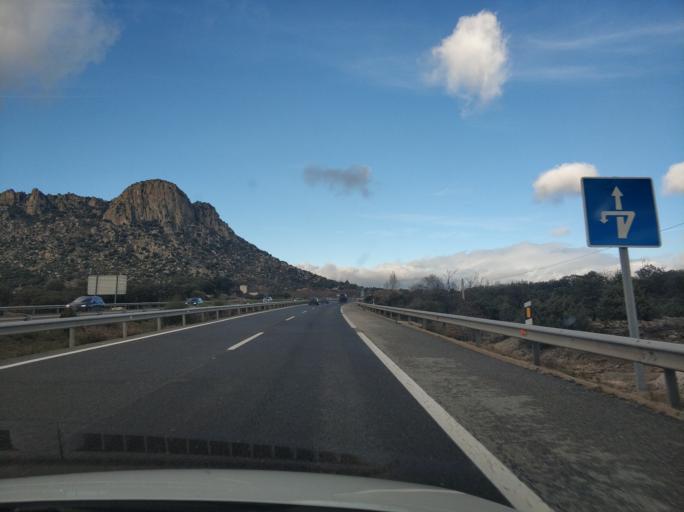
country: ES
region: Madrid
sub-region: Provincia de Madrid
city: La Cabrera
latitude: 40.8671
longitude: -3.6058
